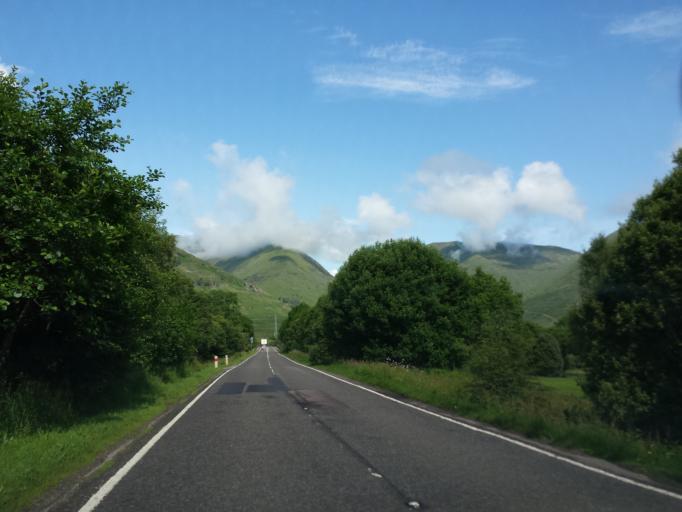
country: GB
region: Scotland
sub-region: Argyll and Bute
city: Garelochhead
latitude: 56.4069
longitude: -5.0162
